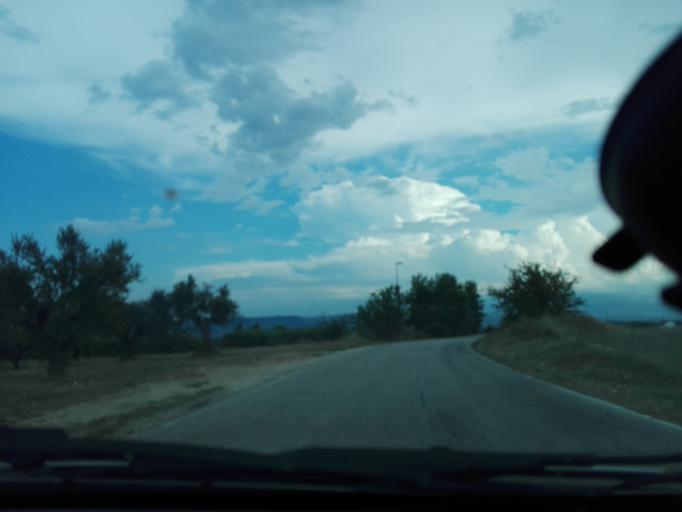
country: IT
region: Abruzzo
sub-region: Provincia di Pescara
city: Cappelle sul Tavo
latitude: 42.4552
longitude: 14.1126
